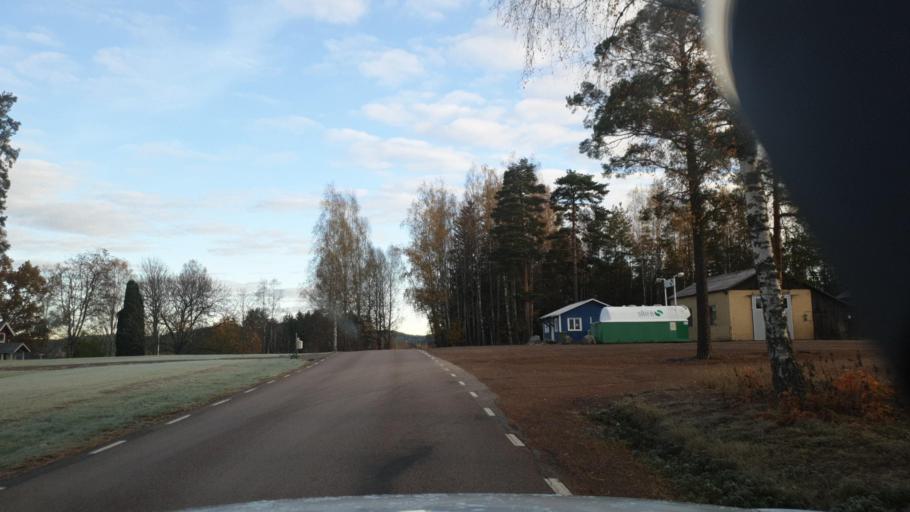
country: SE
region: Vaermland
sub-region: Eda Kommun
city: Charlottenberg
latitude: 59.7842
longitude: 12.2150
